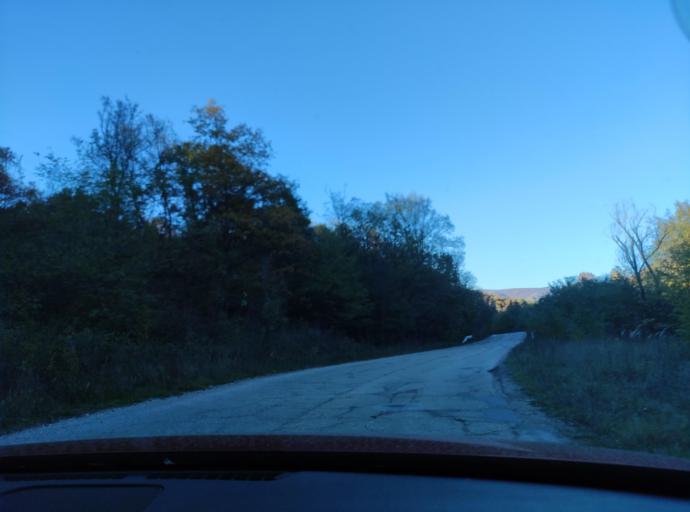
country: BG
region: Montana
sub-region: Obshtina Chiprovtsi
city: Chiprovtsi
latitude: 43.4062
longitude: 22.9378
